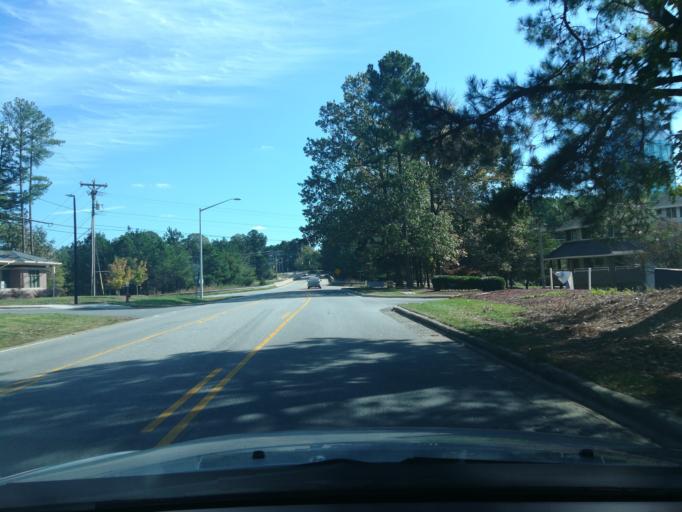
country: US
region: North Carolina
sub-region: Durham County
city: Durham
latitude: 35.9745
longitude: -78.9619
